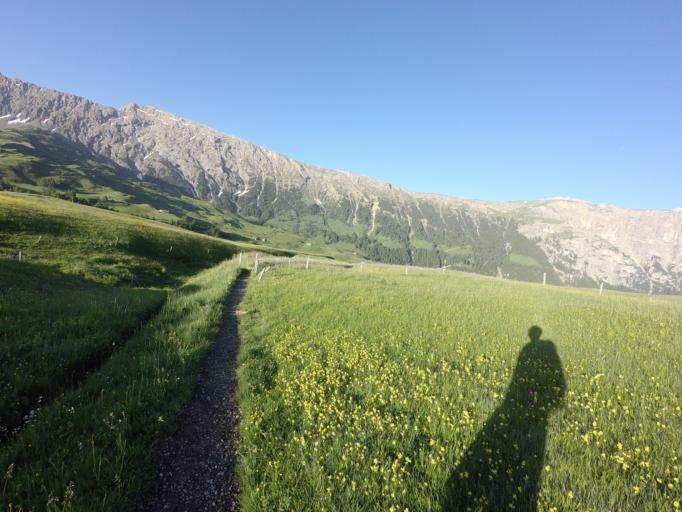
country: IT
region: Trentino-Alto Adige
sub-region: Bolzano
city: Siusi
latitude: 46.5236
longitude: 11.6172
